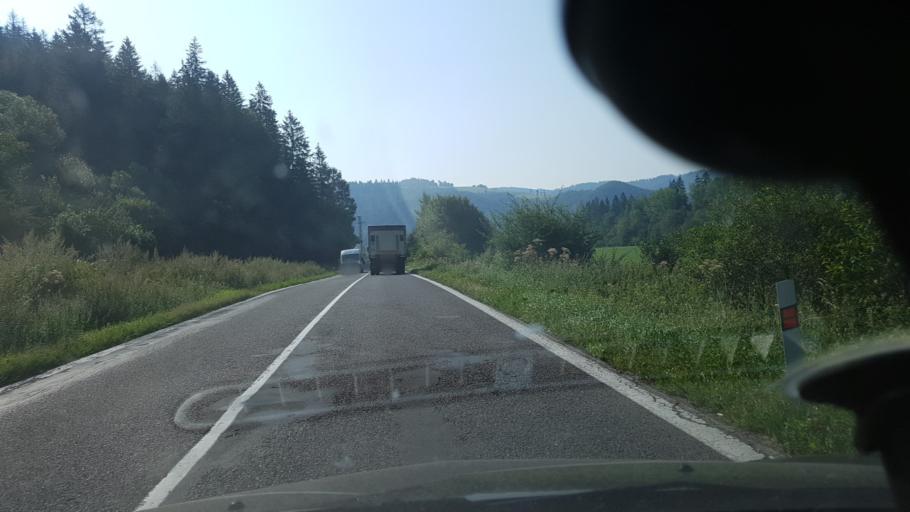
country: SK
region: Zilinsky
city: Tvrdosin
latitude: 49.3001
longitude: 19.4838
